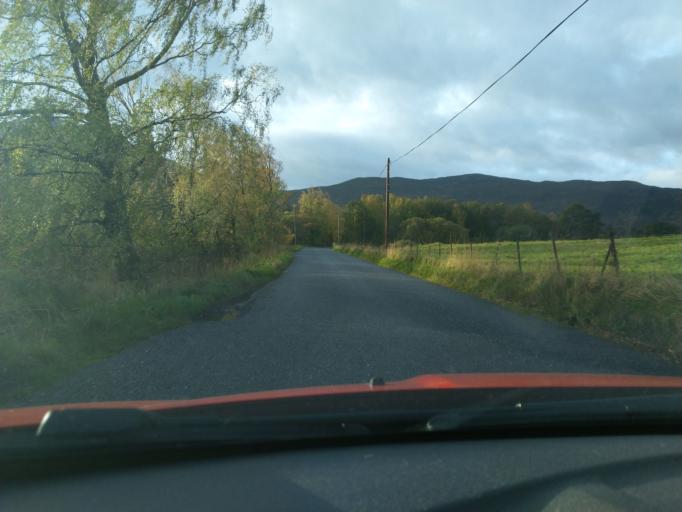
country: GB
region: Scotland
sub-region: Perth and Kinross
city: Aberfeldy
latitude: 56.7029
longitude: -4.1345
